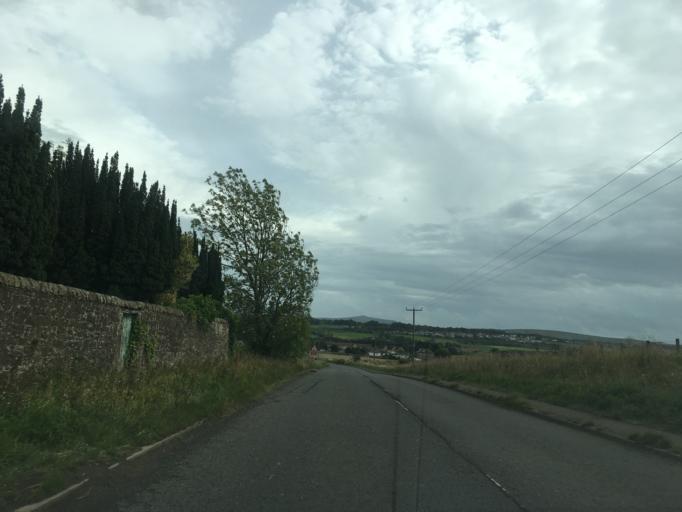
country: GB
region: Scotland
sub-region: West Lothian
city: Kirknewton
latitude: 55.9070
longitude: -3.4071
